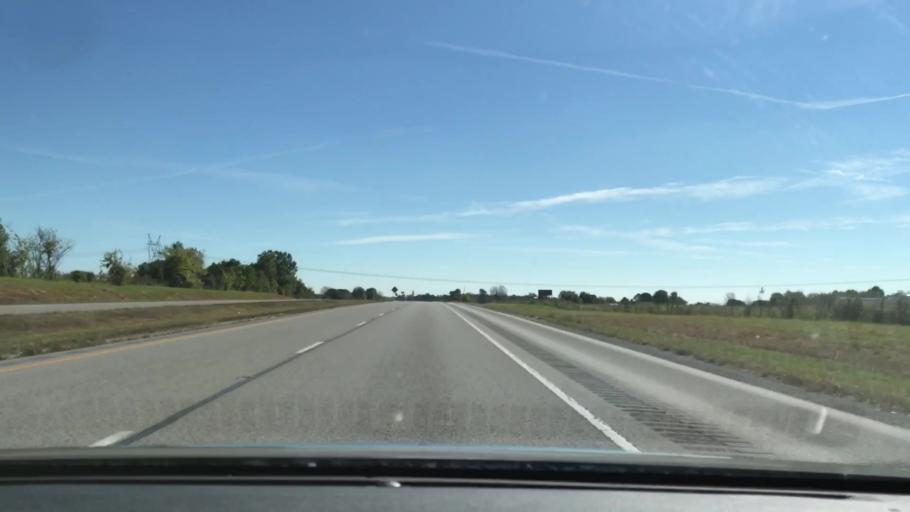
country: US
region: Kentucky
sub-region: Todd County
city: Elkton
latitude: 36.8233
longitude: -87.2030
